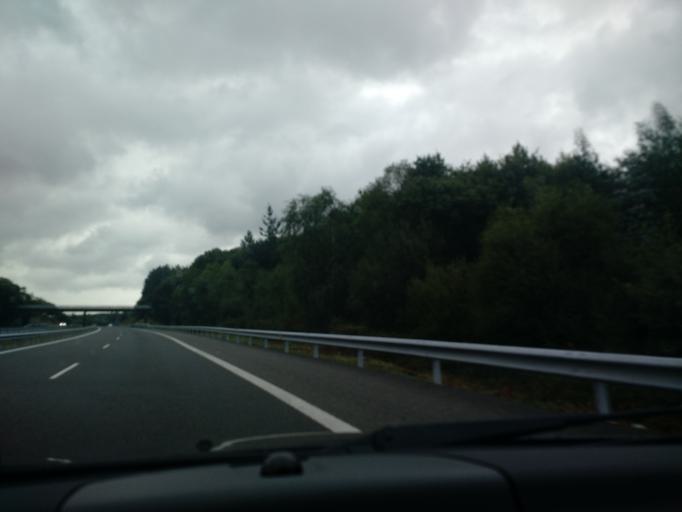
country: ES
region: Galicia
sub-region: Provincia da Coruna
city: Ordes
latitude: 43.0254
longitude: -8.4028
